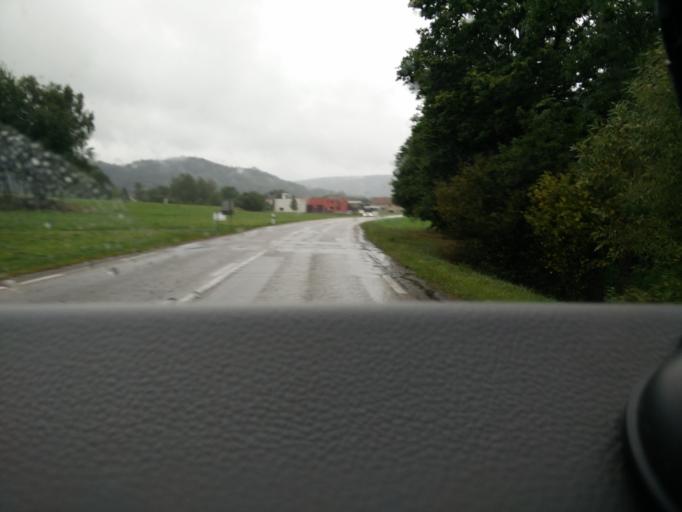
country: FR
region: Lorraine
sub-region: Departement des Vosges
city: Fraize
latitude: 48.1836
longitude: 6.9780
